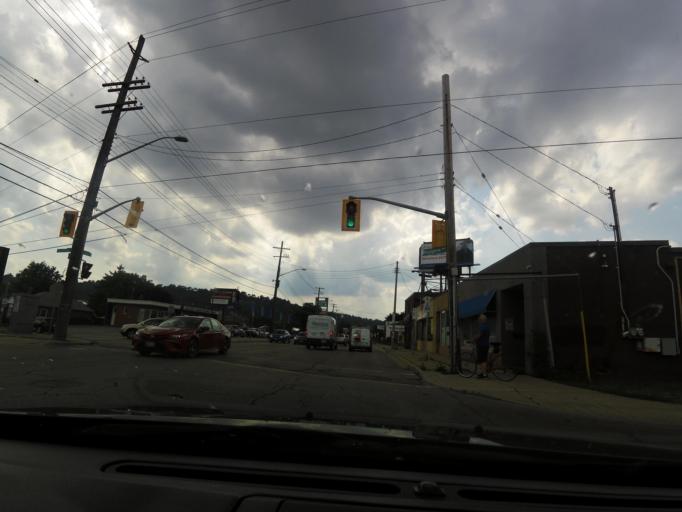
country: CA
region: Ontario
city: Hamilton
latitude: 43.2316
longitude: -79.8052
